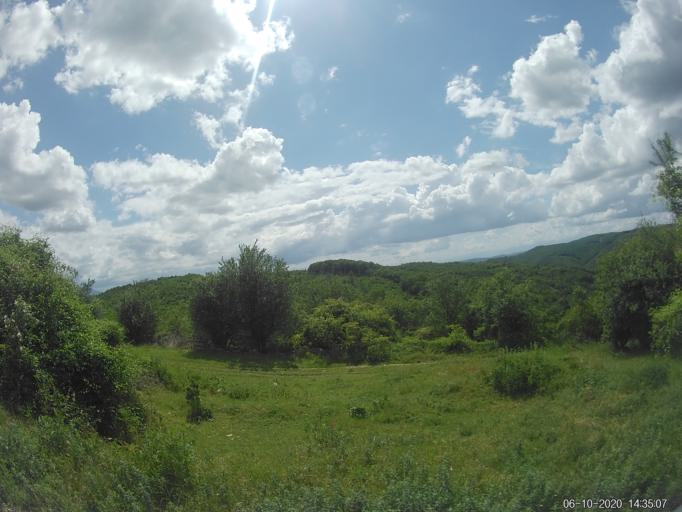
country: XK
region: Prizren
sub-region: Komuna e Therandes
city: Budakovo
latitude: 42.4131
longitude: 20.9330
